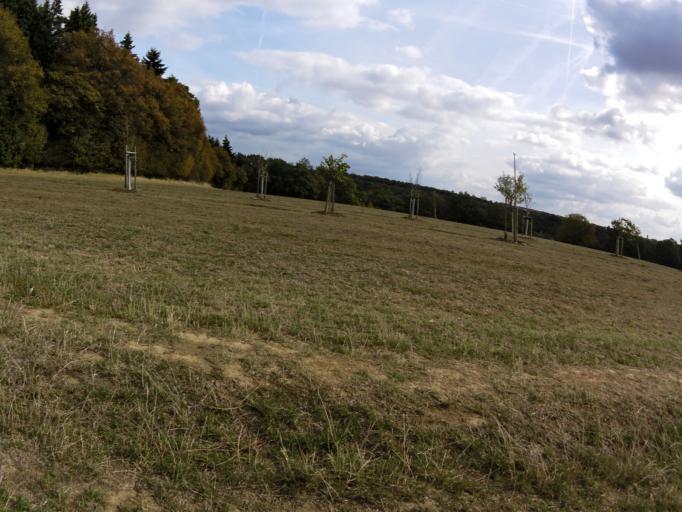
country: DE
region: Bavaria
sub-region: Regierungsbezirk Unterfranken
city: Reichenberg
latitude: 49.7345
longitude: 9.9435
